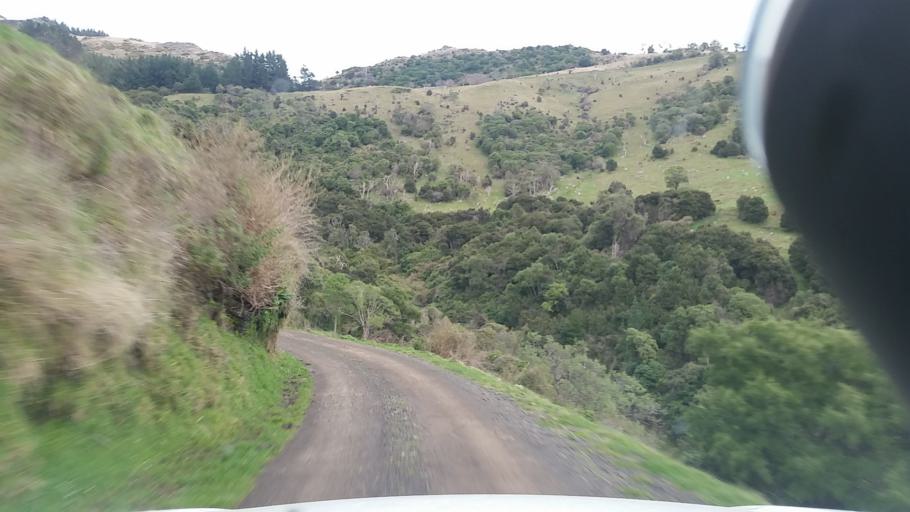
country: NZ
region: Canterbury
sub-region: Christchurch City
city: Christchurch
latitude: -43.8190
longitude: 172.9901
